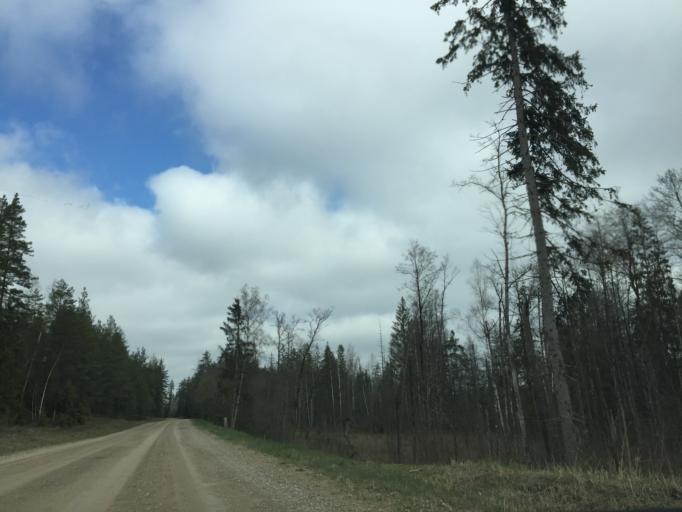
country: EE
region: Valgamaa
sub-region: Valga linn
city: Valga
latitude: 57.6191
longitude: 26.2361
